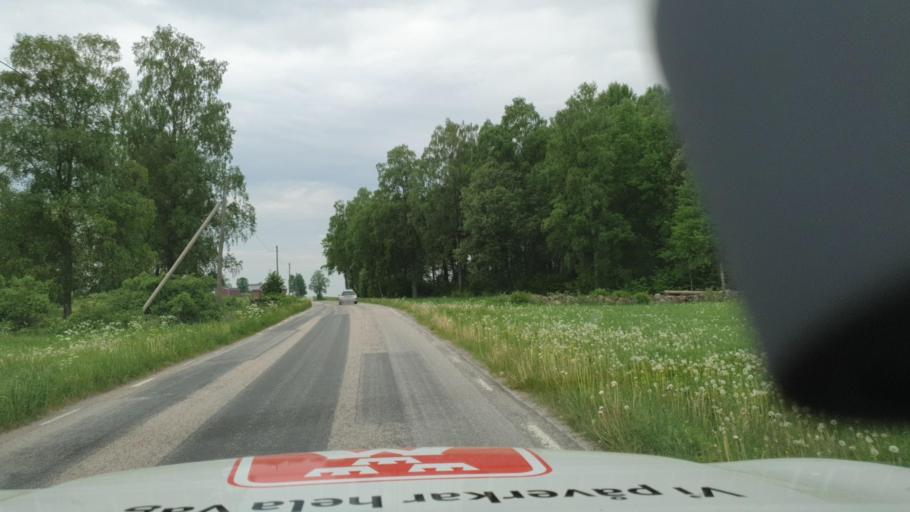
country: SE
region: Vaestra Goetaland
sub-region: Ulricehamns Kommun
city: Ulricehamn
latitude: 57.9172
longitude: 13.3611
